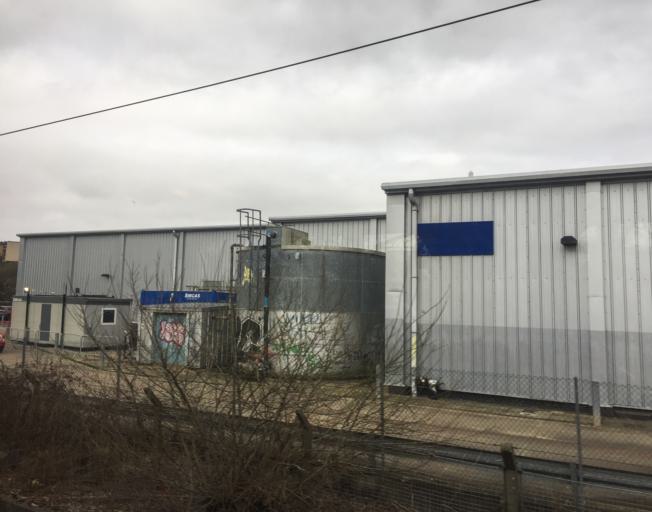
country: GB
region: Scotland
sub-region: West Dunbartonshire
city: Clydebank
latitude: 55.9057
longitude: -4.3999
